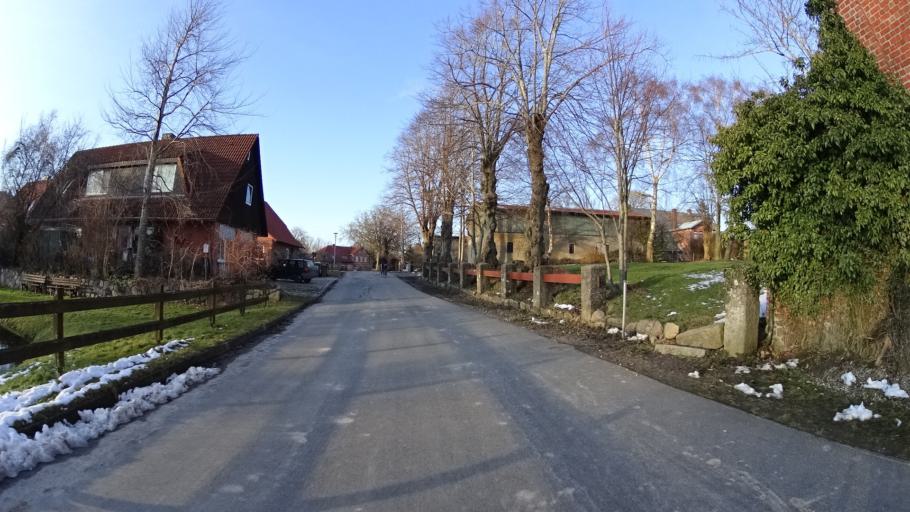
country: DE
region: Schleswig-Holstein
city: Bendfeld
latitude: 54.3627
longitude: 10.4195
